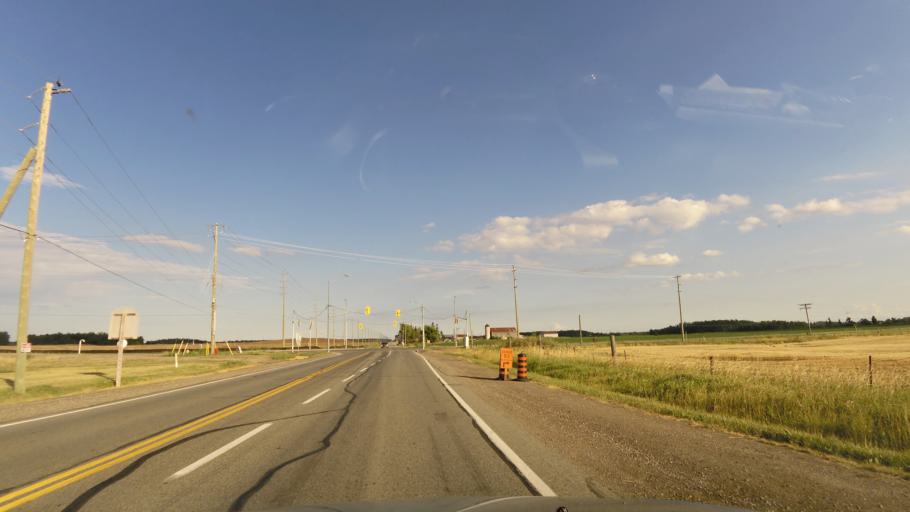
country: CA
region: Ontario
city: Brampton
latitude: 43.6954
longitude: -79.8683
